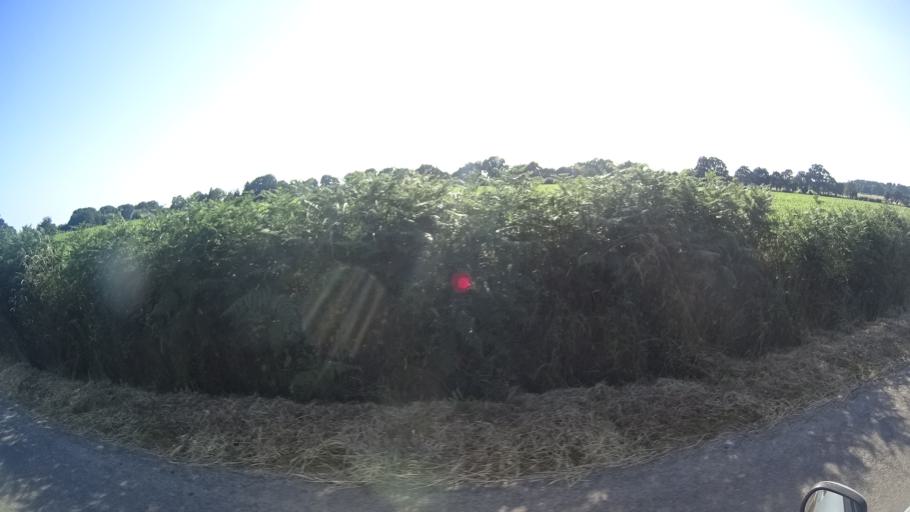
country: FR
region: Brittany
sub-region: Departement du Morbihan
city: Rieux
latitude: 47.5950
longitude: -2.1241
